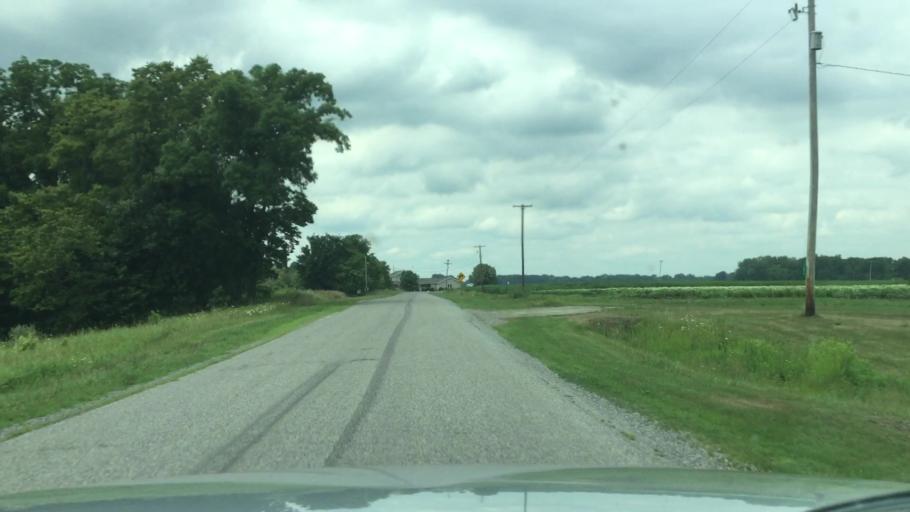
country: US
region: Michigan
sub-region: Saginaw County
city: Burt
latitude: 43.2606
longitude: -83.8782
